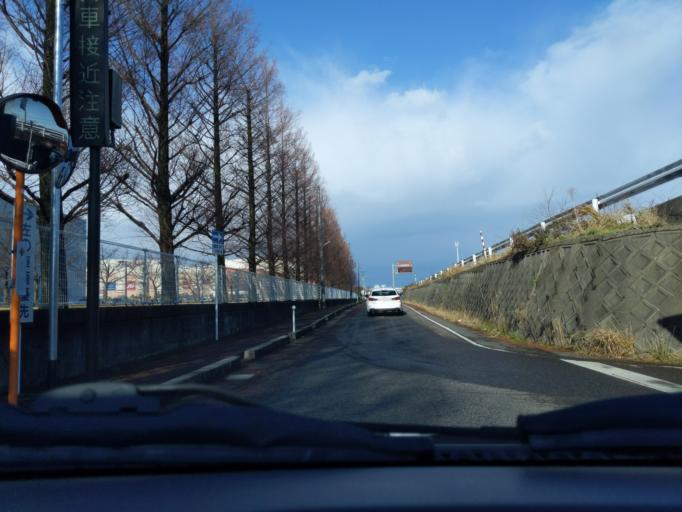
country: JP
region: Niigata
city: Kameda-honcho
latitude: 37.8745
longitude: 139.0850
